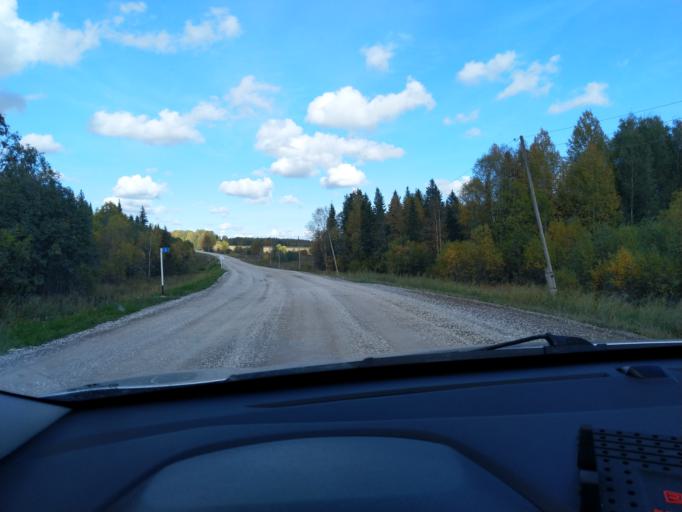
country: RU
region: Perm
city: Usol'ye
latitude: 59.4647
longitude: 56.3699
